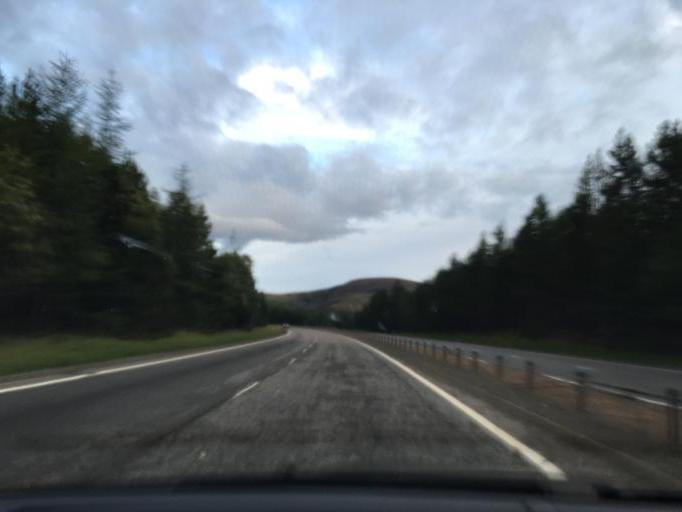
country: GB
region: Scotland
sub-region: Highland
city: Inverness
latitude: 57.3902
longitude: -4.1225
